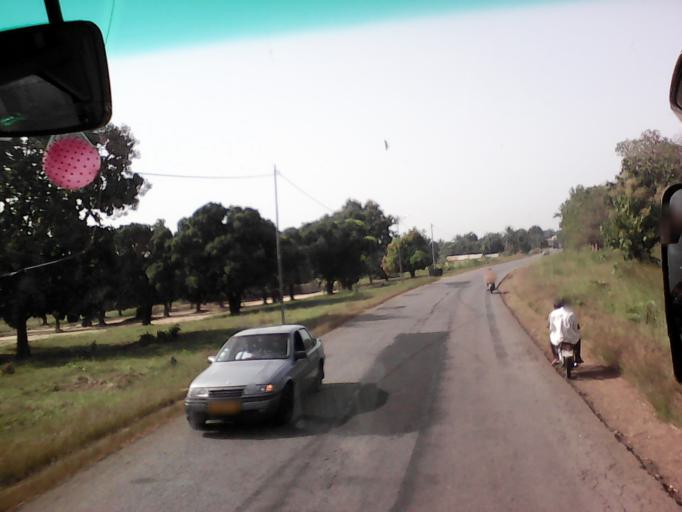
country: TG
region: Centrale
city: Sokode
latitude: 9.1049
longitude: 1.1432
